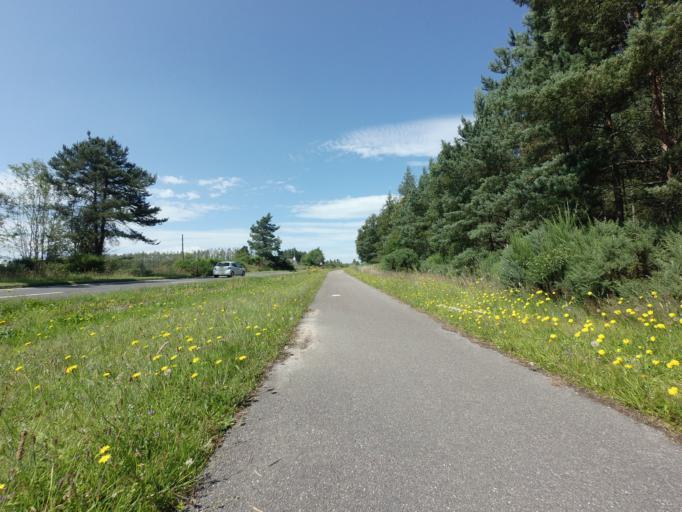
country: GB
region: Scotland
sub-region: Highland
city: Conon Bridge
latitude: 57.5402
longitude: -4.3726
